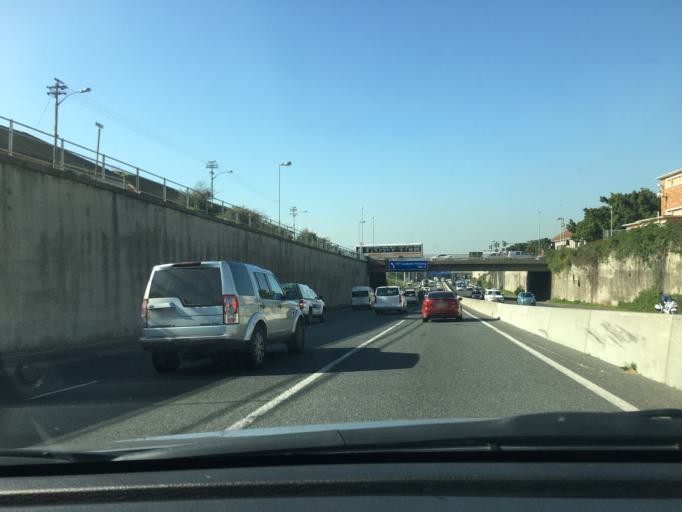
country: ZA
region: Western Cape
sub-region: City of Cape Town
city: Rosebank
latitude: -33.9460
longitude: 18.4686
